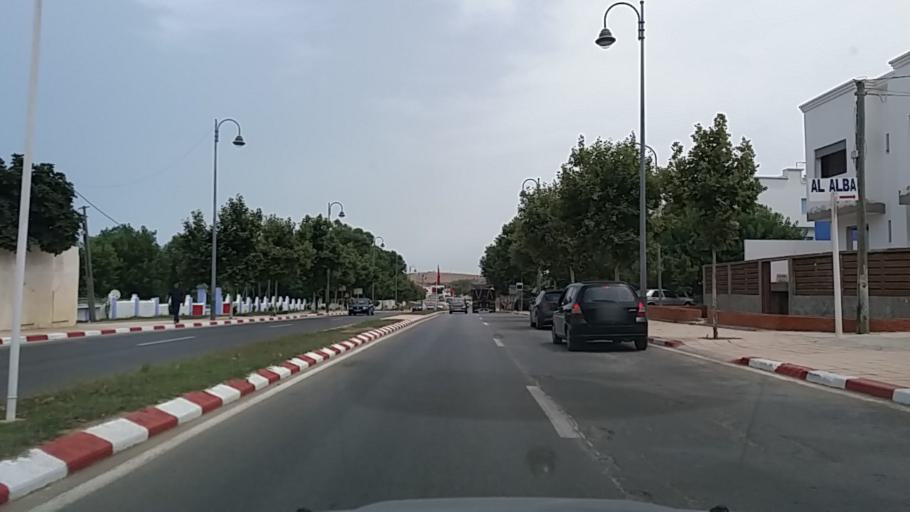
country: MA
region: Tanger-Tetouan
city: Asilah
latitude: 35.4712
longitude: -6.0287
